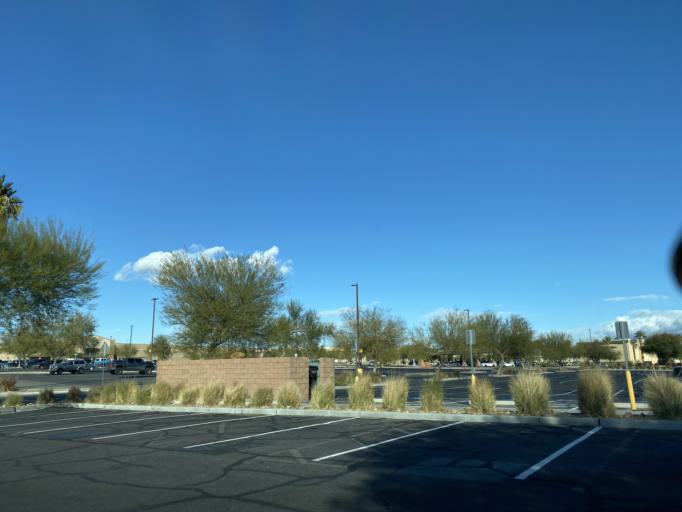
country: US
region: Nevada
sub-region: Clark County
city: Las Vegas
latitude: 36.2716
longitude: -115.2680
